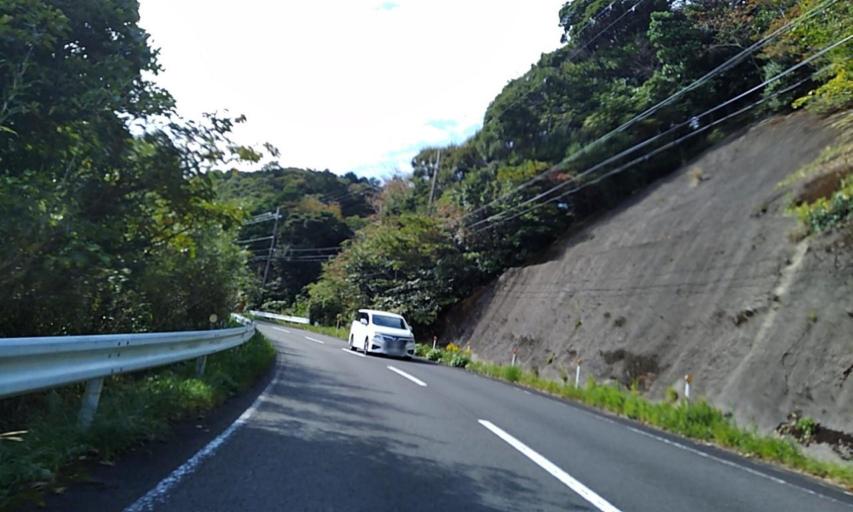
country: JP
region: Wakayama
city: Shingu
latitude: 33.4690
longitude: 135.8318
